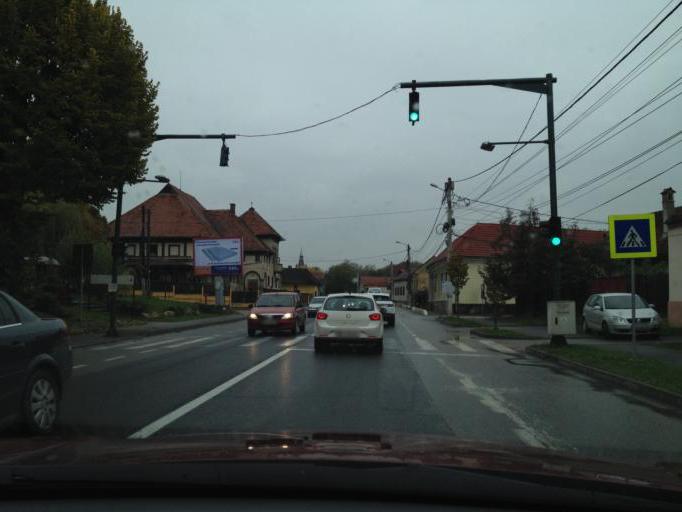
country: RO
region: Brasov
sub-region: Comuna Cristian
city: Cristian
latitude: 45.6299
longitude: 25.4868
